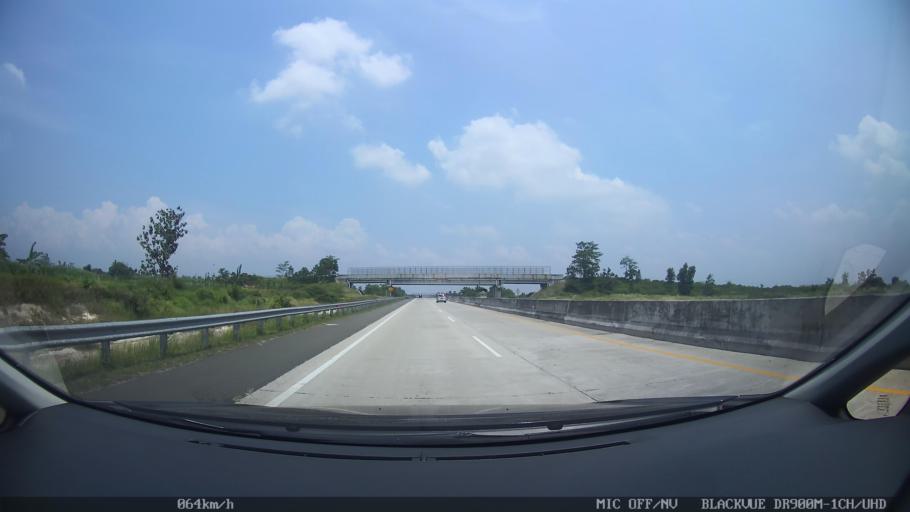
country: ID
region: Lampung
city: Kedaton
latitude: -5.3415
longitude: 105.3121
